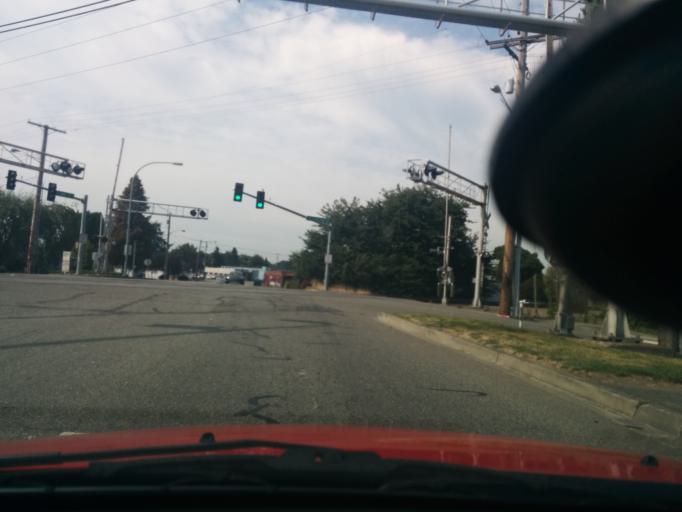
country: US
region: Washington
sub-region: Skagit County
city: Mount Vernon
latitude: 48.4065
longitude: -122.3357
